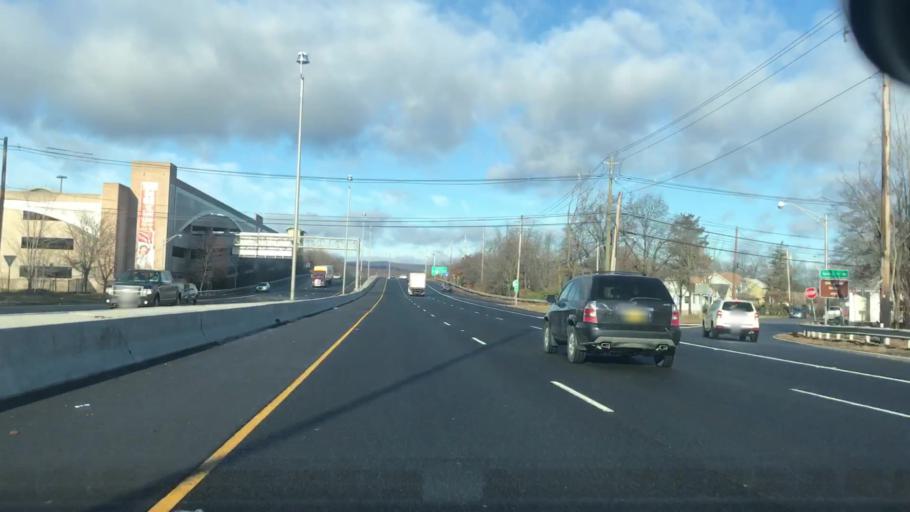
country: US
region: New Jersey
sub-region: Bergen County
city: Mahwah
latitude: 41.0734
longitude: -74.1424
